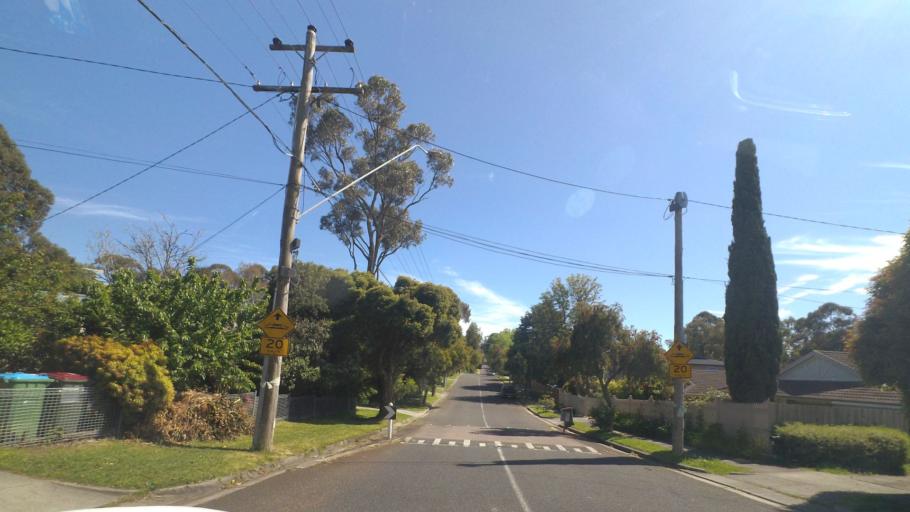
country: AU
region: Victoria
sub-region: Maroondah
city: Heathmont
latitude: -37.8252
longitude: 145.2578
